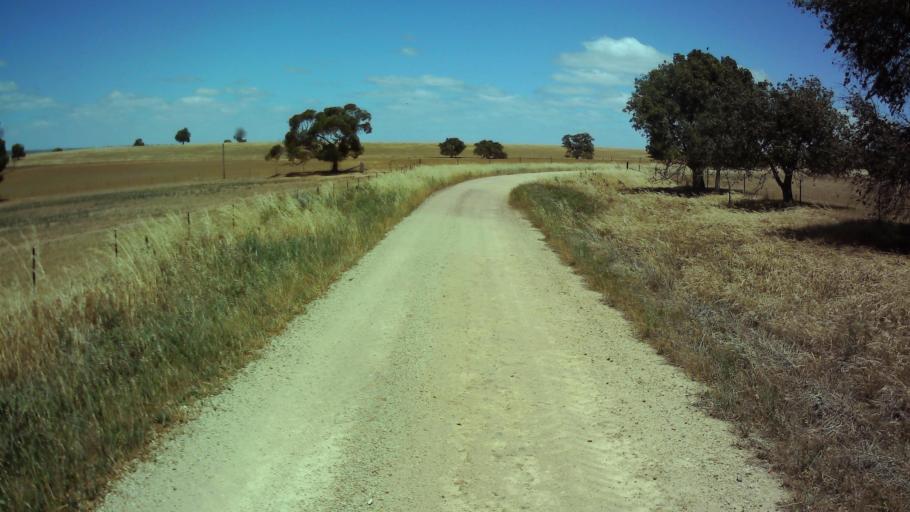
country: AU
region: New South Wales
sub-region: Weddin
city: Grenfell
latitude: -33.9530
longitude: 148.3690
